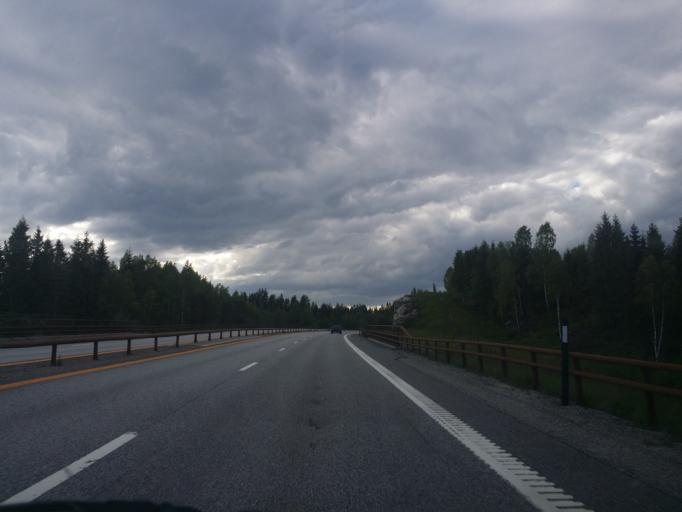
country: NO
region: Akershus
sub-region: Eidsvoll
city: Raholt
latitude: 60.2701
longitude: 11.1582
